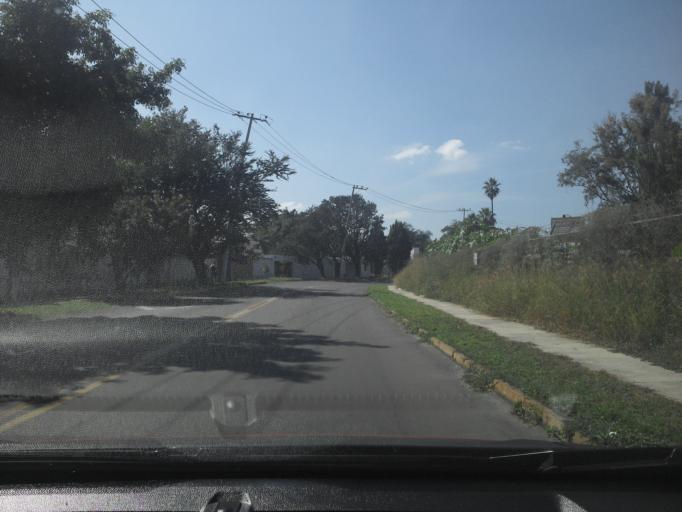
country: MX
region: Jalisco
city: Zapopan2
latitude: 20.6922
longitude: -103.4055
